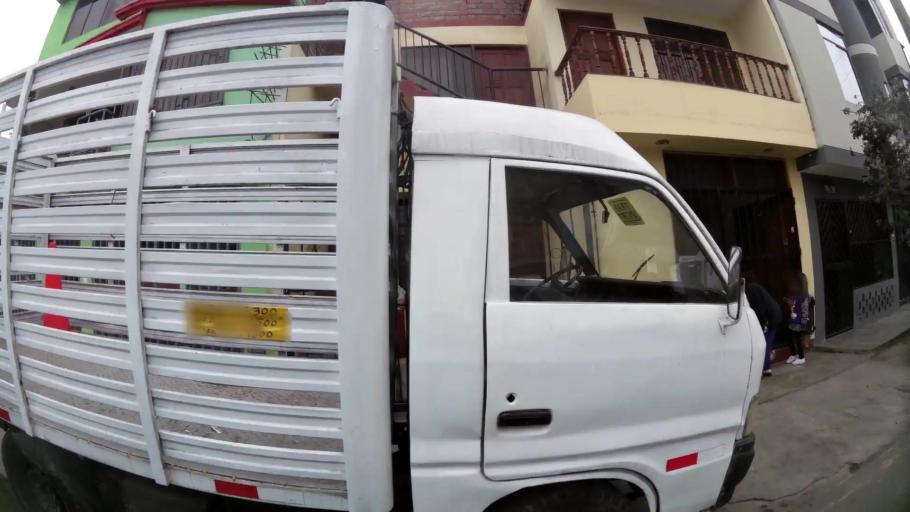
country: PE
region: Lima
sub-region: Lima
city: Surco
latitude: -12.1728
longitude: -76.9655
